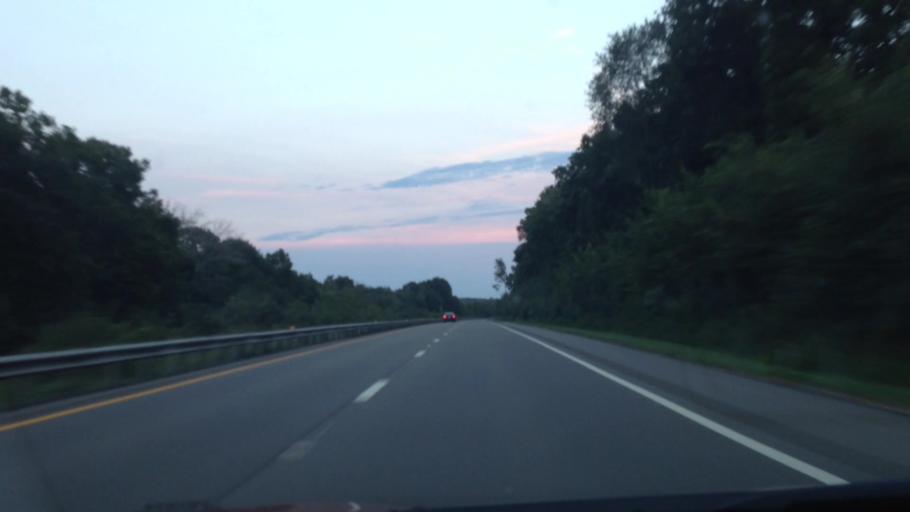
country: US
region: Ohio
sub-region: Stark County
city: Canal Fulton
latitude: 40.8510
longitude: -81.5675
